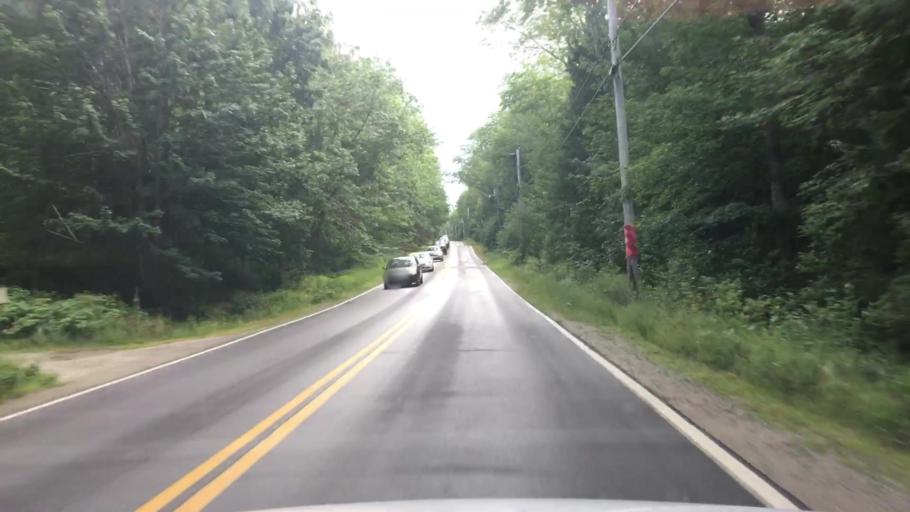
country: US
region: Maine
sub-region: Hancock County
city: Trenton
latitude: 44.4586
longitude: -68.4249
